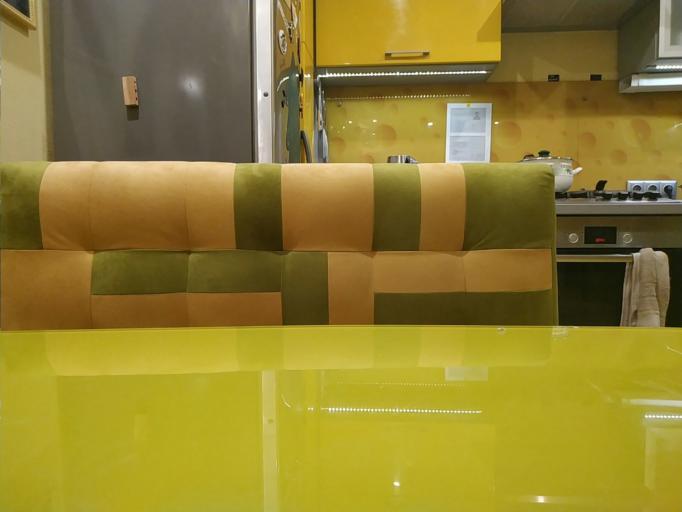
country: RU
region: Murmansk
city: Alakurtti
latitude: 66.3107
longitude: 30.2396
